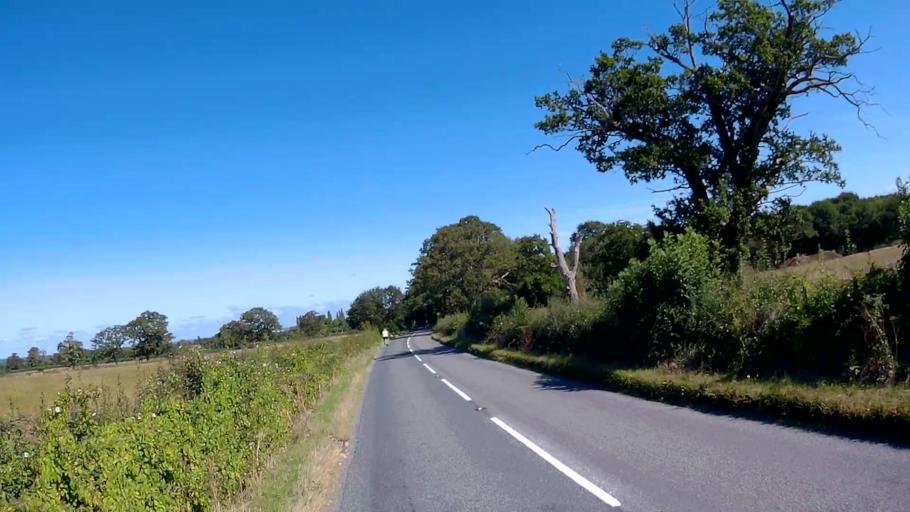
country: GB
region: England
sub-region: Wokingham
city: Swallowfield
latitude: 51.3776
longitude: -0.9953
